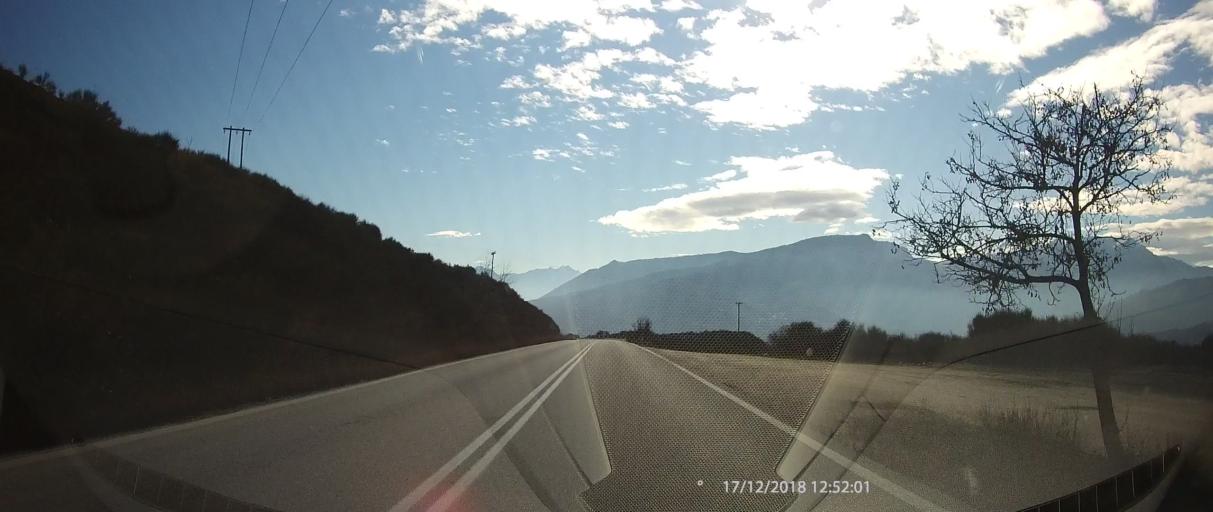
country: GR
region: Thessaly
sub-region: Trikala
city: Kastraki
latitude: 39.7602
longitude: 21.4738
